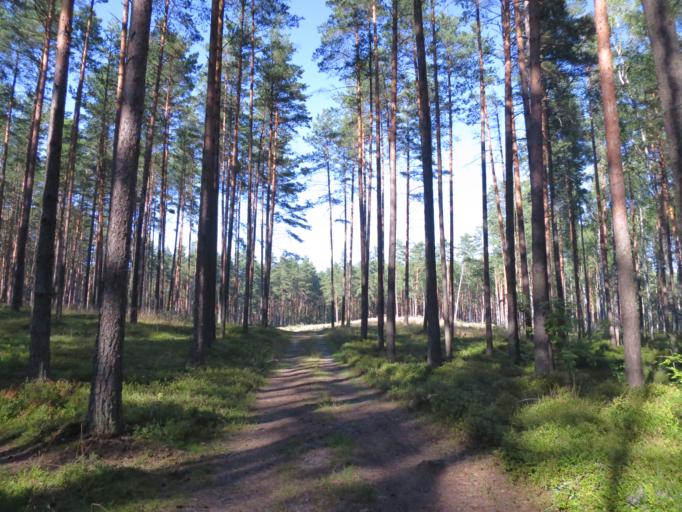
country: LV
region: Riga
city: Jaunciems
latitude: 57.0719
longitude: 24.1995
